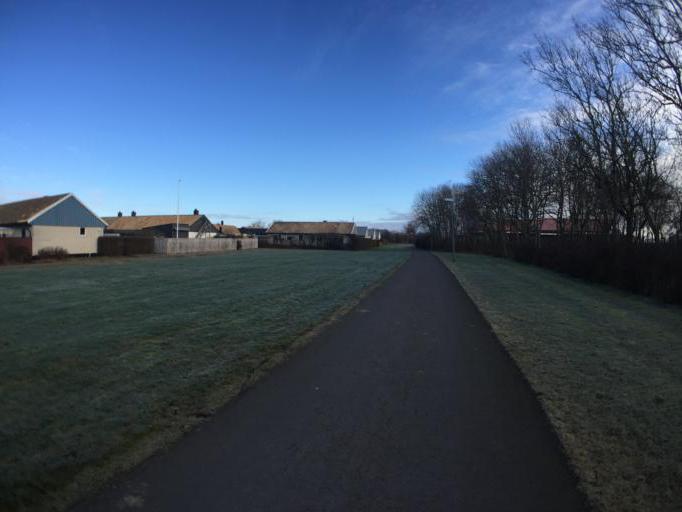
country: SE
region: Skane
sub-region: Hoganas Kommun
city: Hoganas
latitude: 56.1501
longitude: 12.5797
